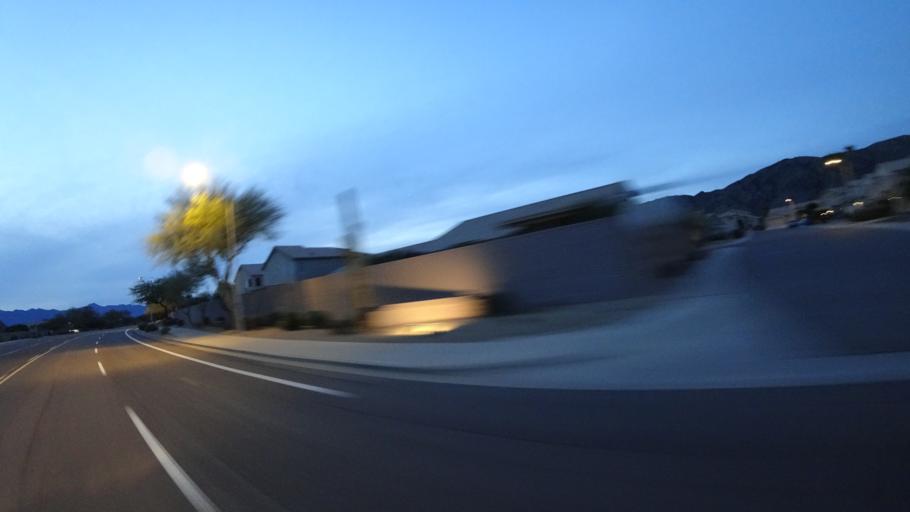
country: US
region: Arizona
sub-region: Maricopa County
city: Laveen
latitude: 33.3037
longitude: -112.0834
